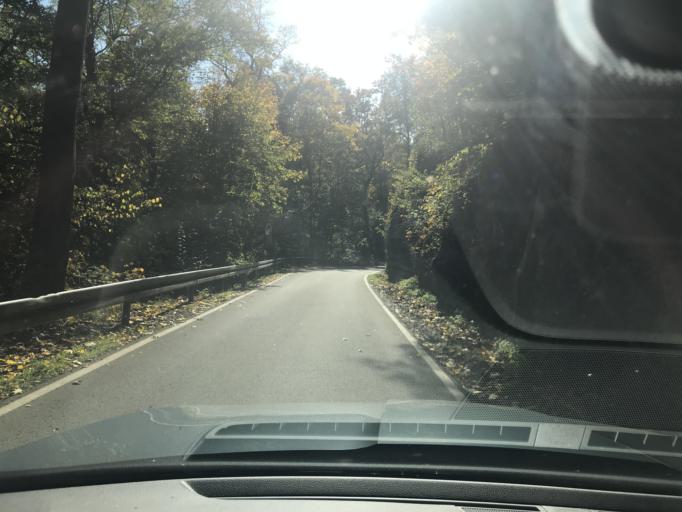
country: DE
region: Saxony-Anhalt
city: Timmenrode
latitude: 51.7184
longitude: 10.9730
